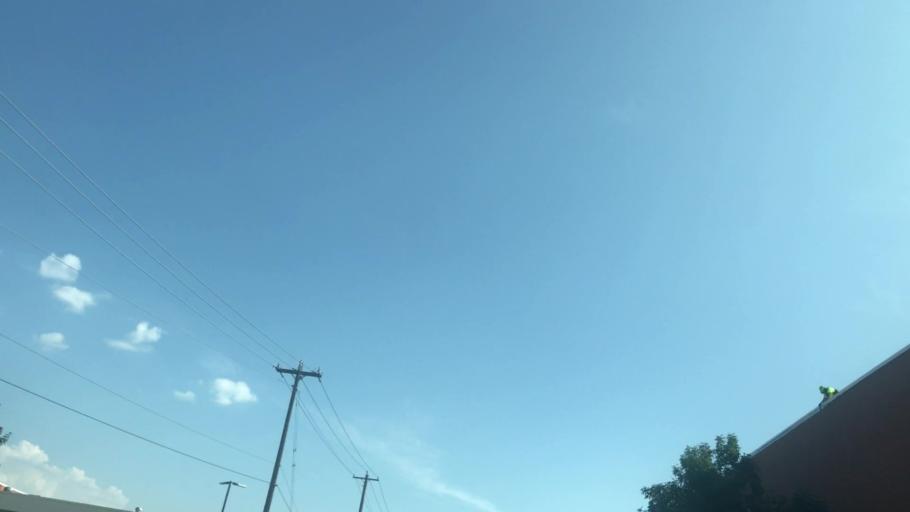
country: US
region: Wisconsin
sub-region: Brown County
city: Allouez
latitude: 44.4927
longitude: -88.0374
